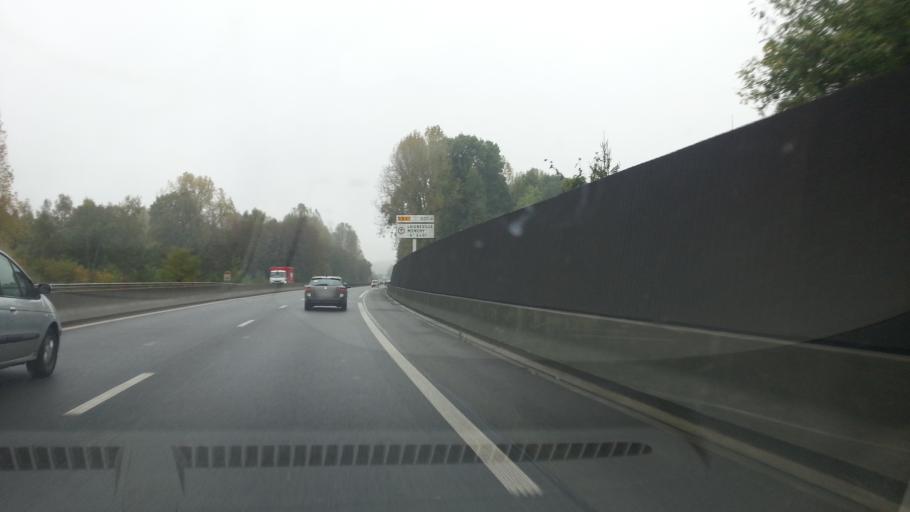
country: FR
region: Picardie
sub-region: Departement de l'Oise
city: Cauffry
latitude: 49.3065
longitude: 2.4531
